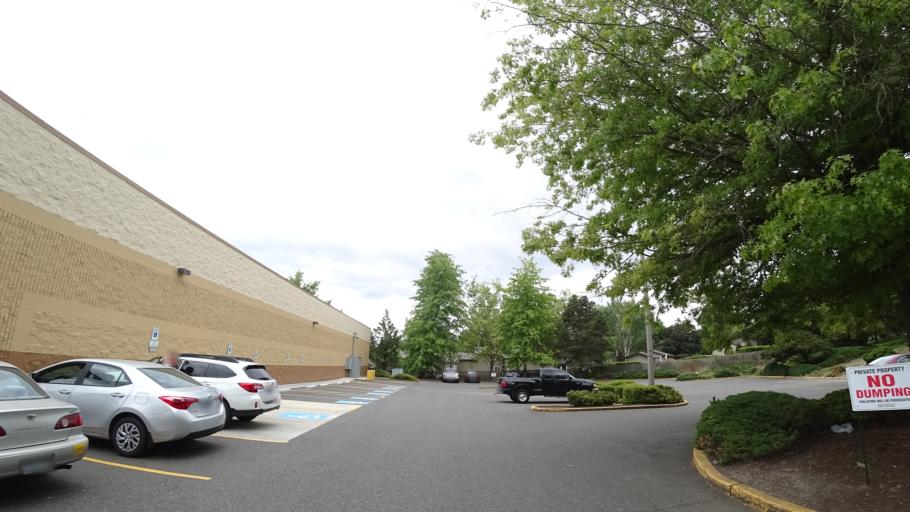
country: US
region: Oregon
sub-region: Washington County
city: Beaverton
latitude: 45.4607
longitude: -122.7972
